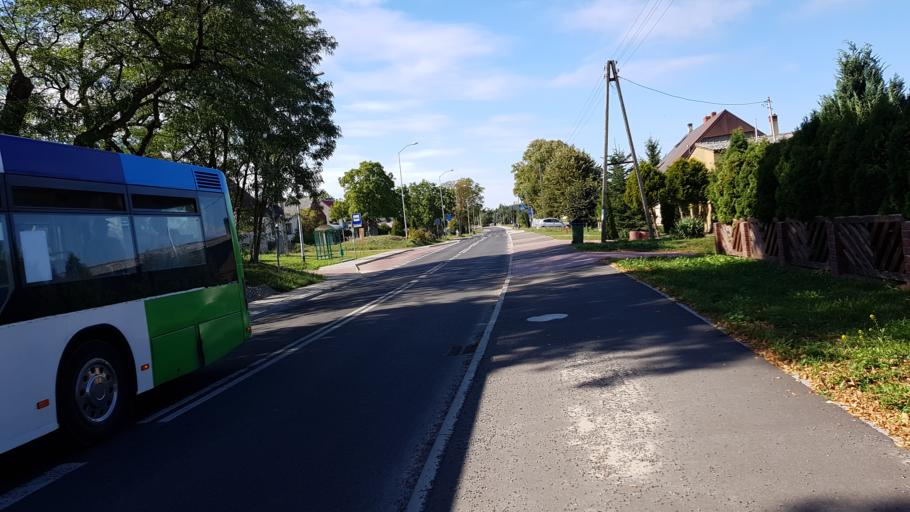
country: PL
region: West Pomeranian Voivodeship
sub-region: Powiat policki
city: Przeclaw
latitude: 53.3497
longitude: 14.4760
